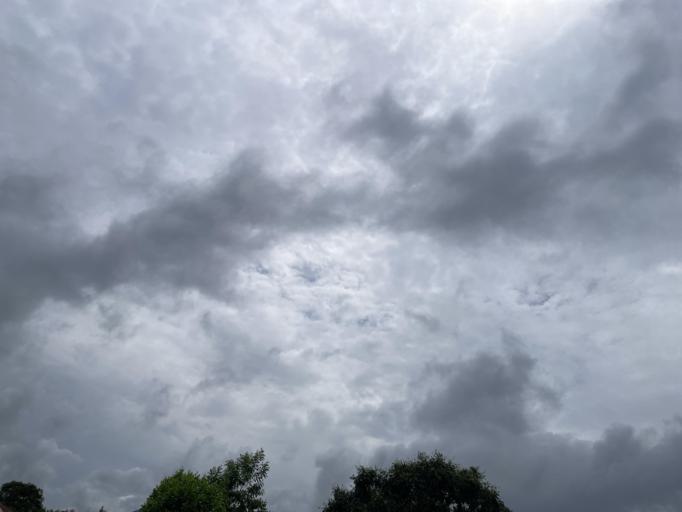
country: SL
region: Northern Province
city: Kambia
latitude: 9.1311
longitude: -12.9057
